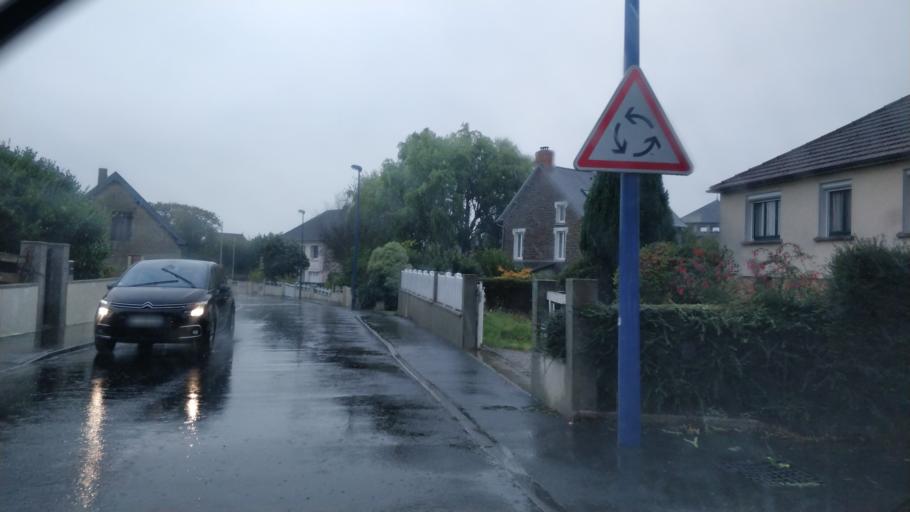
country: FR
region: Lower Normandy
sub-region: Departement de la Manche
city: Brehal
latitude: 48.8990
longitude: -1.5102
